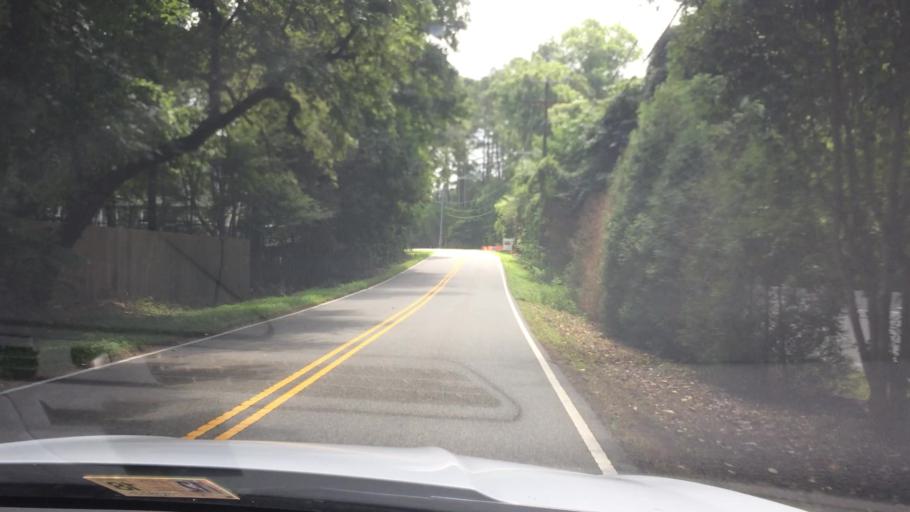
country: US
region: Virginia
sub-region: City of Poquoson
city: Poquoson
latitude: 37.1383
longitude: -76.4544
